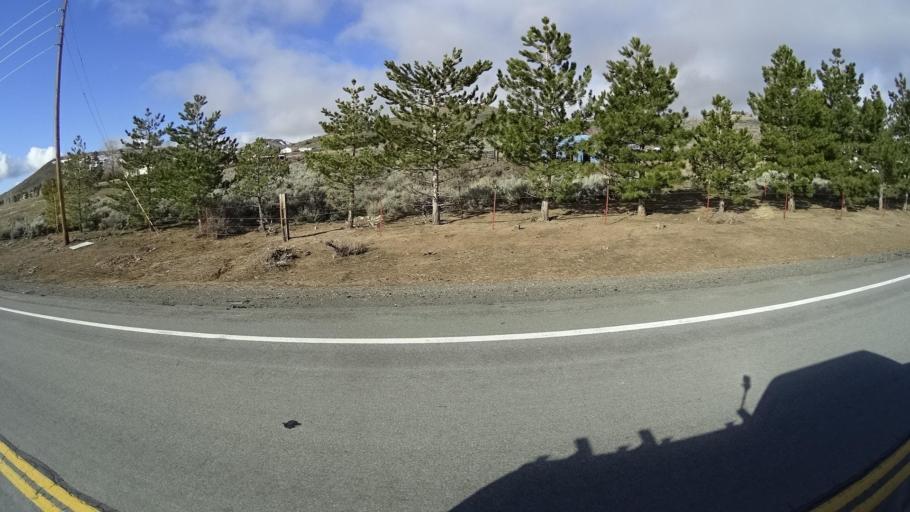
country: US
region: Nevada
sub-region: Washoe County
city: Cold Springs
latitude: 39.7871
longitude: -119.8991
